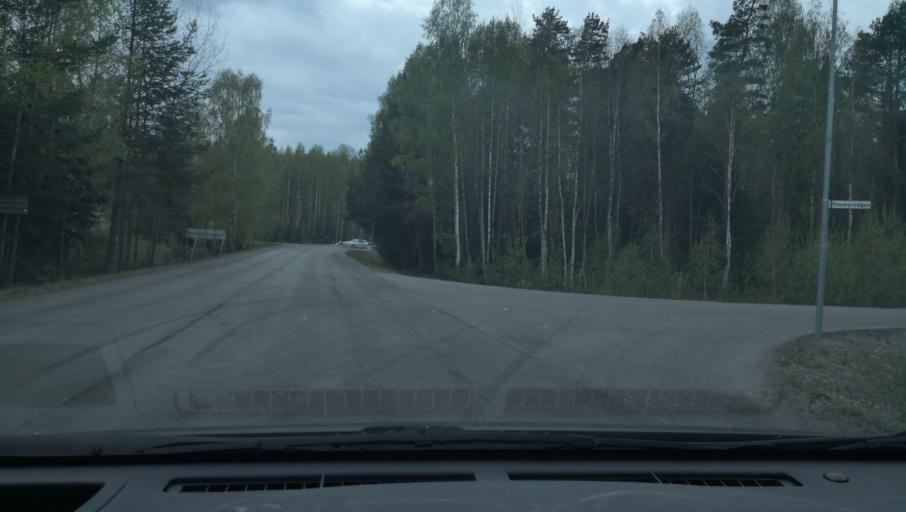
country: SE
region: Dalarna
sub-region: Avesta Kommun
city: Avesta
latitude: 60.1473
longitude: 16.2296
